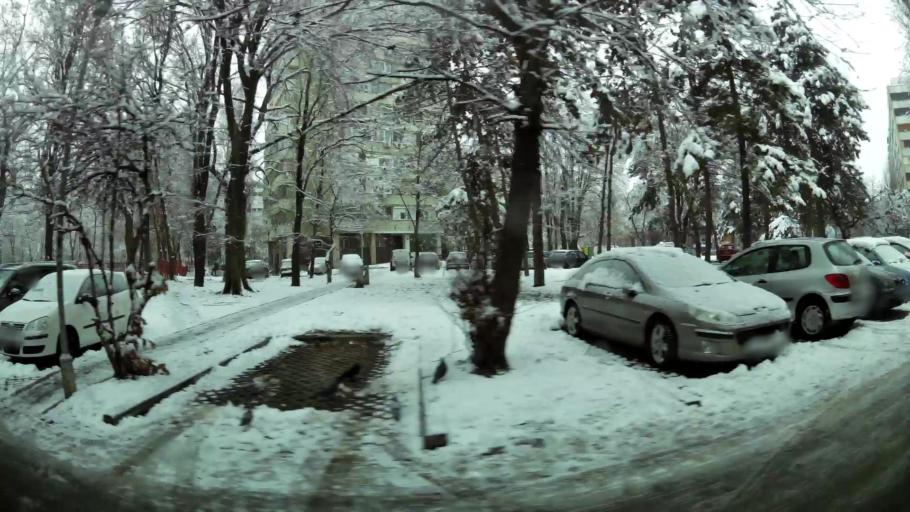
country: RS
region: Central Serbia
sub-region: Belgrade
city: Zemun
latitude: 44.8236
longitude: 20.4077
